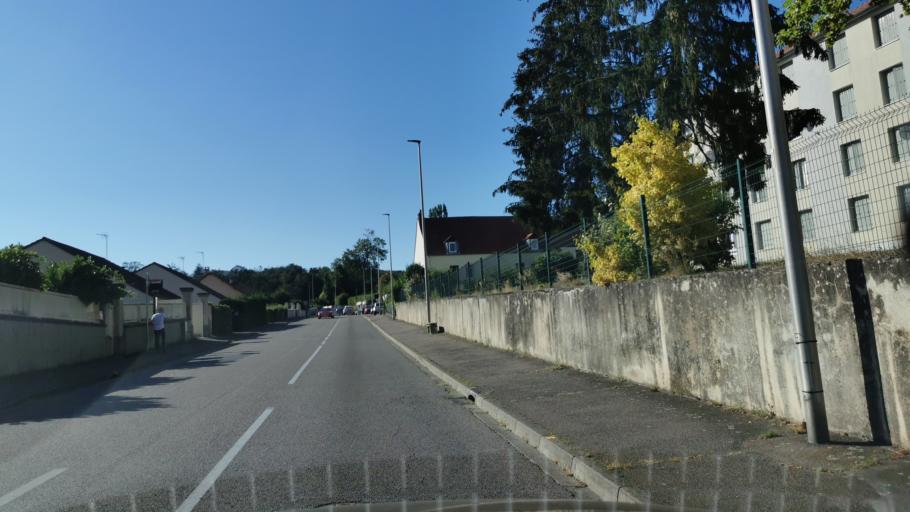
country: FR
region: Bourgogne
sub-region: Departement de Saone-et-Loire
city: Le Creusot
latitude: 46.7998
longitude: 4.4153
